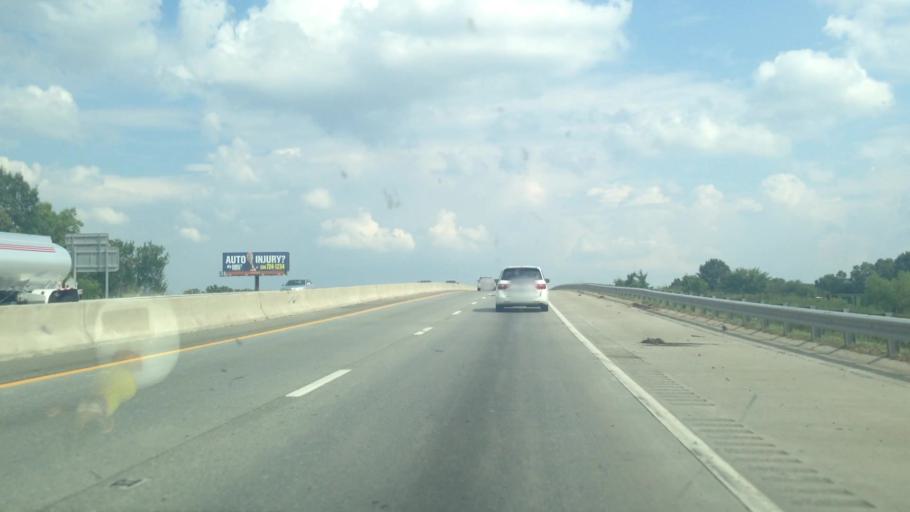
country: US
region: North Carolina
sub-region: Forsyth County
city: Winston-Salem
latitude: 36.1303
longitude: -80.2360
